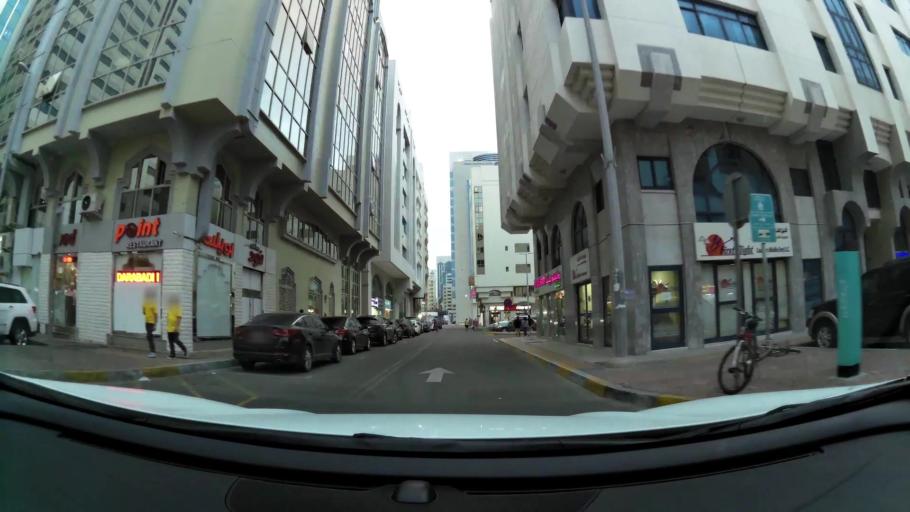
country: AE
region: Abu Dhabi
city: Abu Dhabi
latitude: 24.4915
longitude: 54.3739
